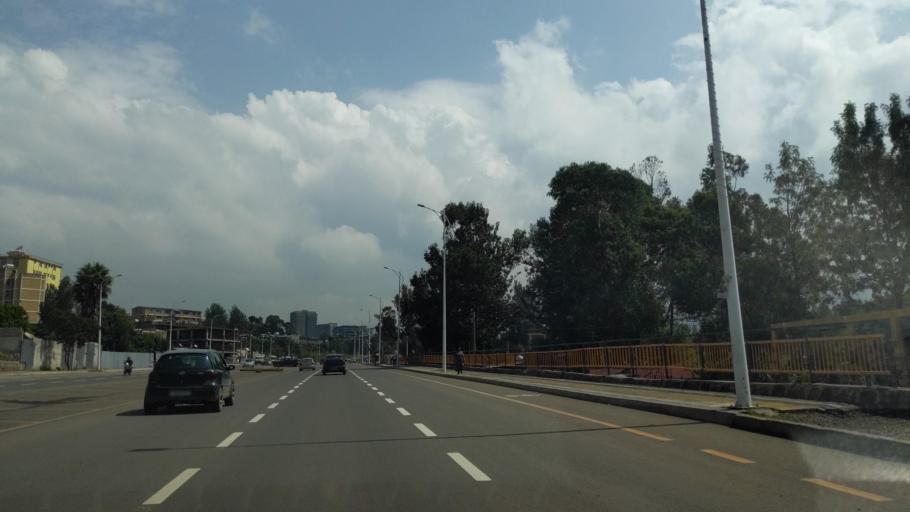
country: ET
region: Adis Abeba
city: Addis Ababa
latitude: 9.0018
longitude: 38.7736
